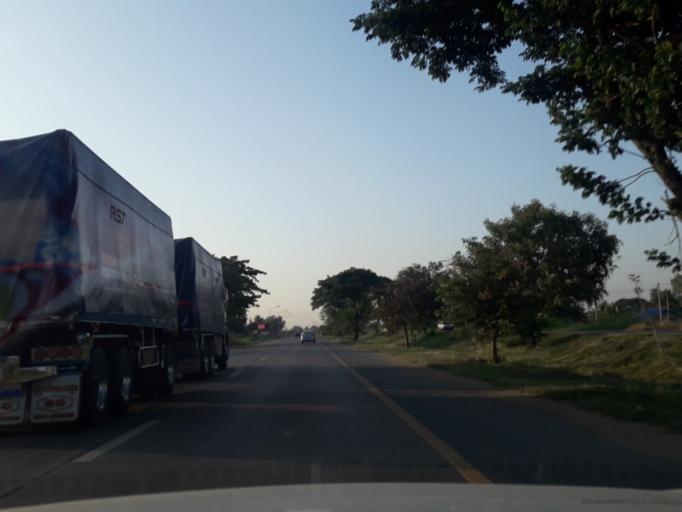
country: TH
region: Phra Nakhon Si Ayutthaya
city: Bang Pa-in
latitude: 14.2326
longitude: 100.5394
